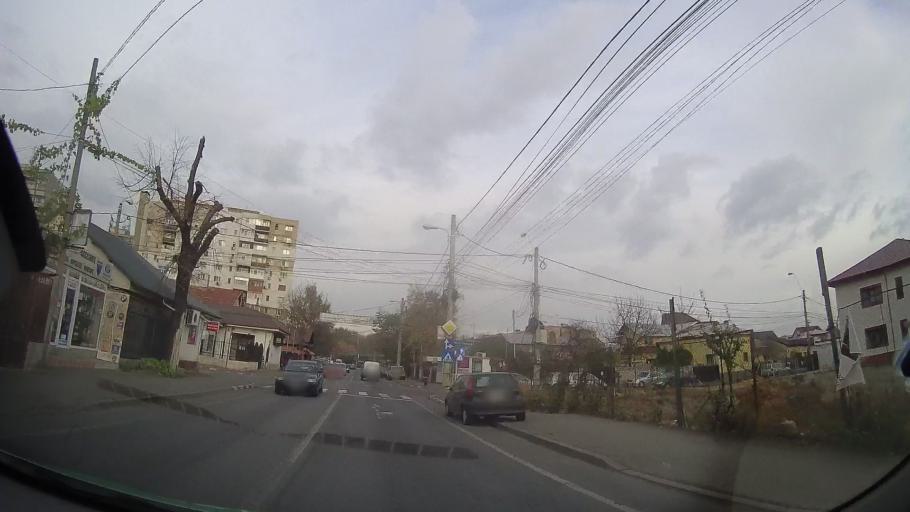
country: RO
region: Prahova
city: Ploiesti
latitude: 44.9443
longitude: 26.0334
